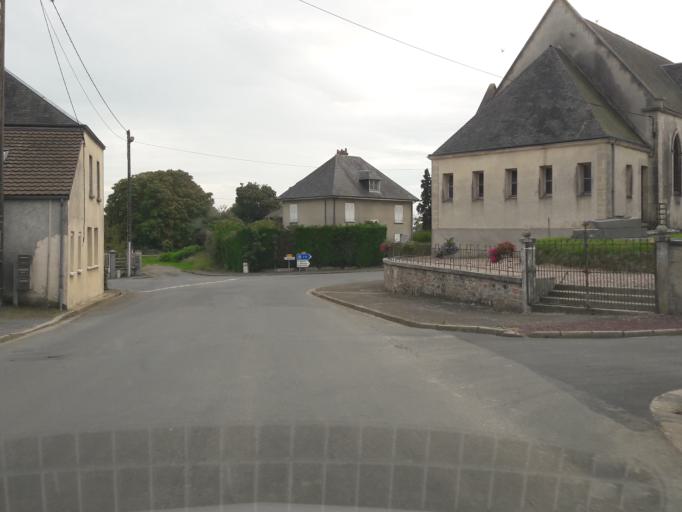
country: FR
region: Lower Normandy
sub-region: Departement du Calvados
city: Cahagnes
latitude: 49.0768
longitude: -0.8190
